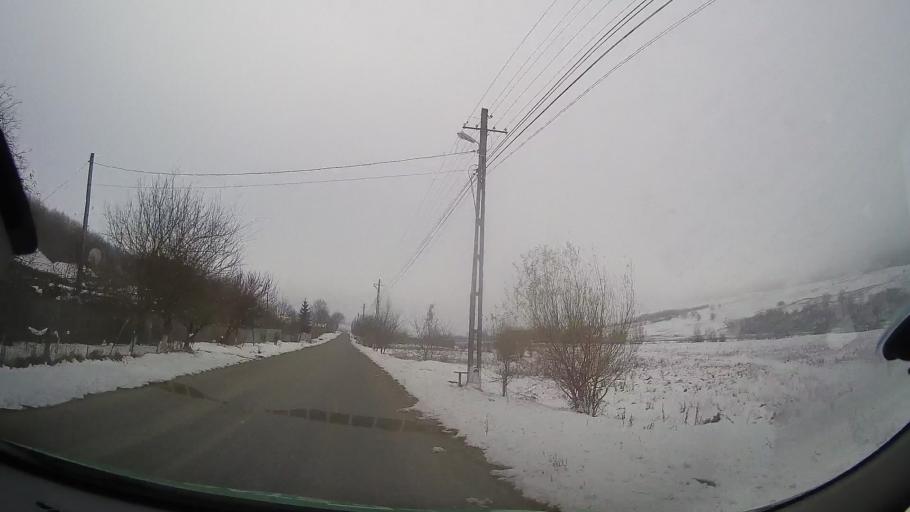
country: RO
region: Bacau
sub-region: Comuna Vultureni
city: Vultureni
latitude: 46.3240
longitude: 27.2922
